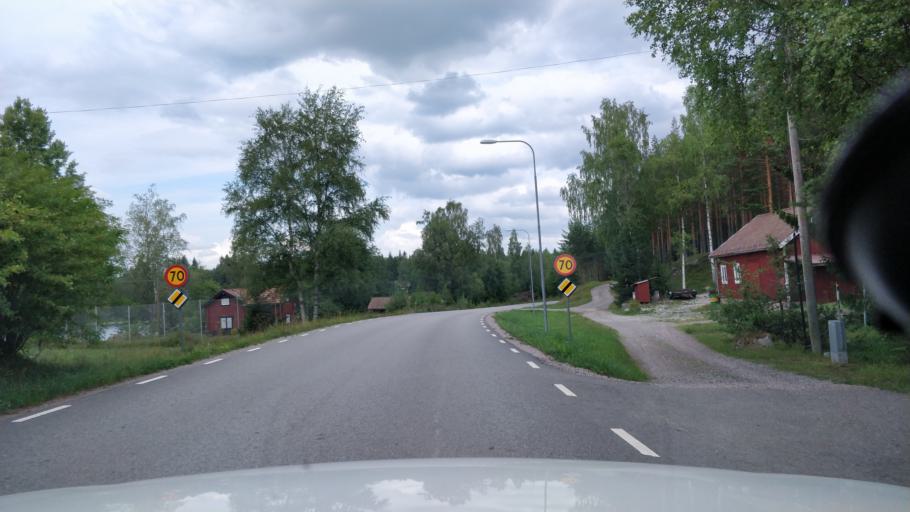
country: SE
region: Dalarna
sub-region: Faluns Kommun
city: Bjursas
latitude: 60.7464
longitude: 15.4701
